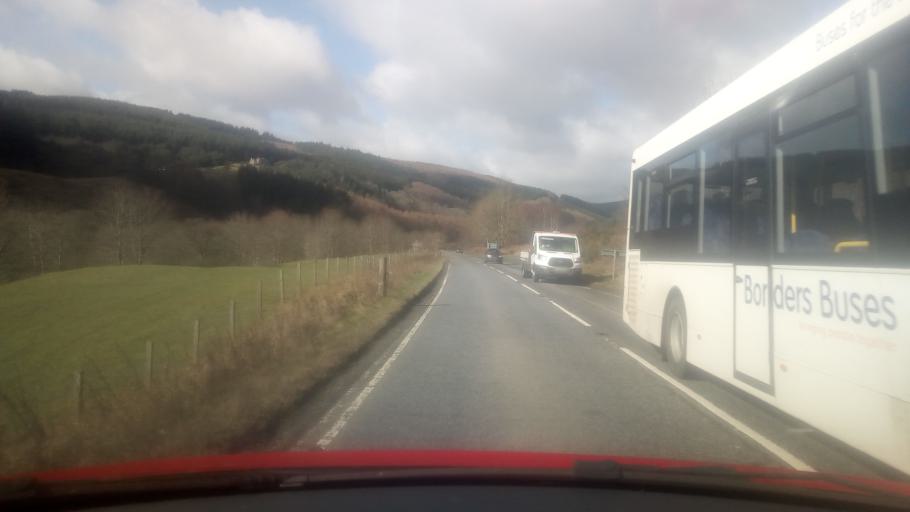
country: GB
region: Scotland
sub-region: The Scottish Borders
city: Innerleithen
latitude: 55.6171
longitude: -2.9449
